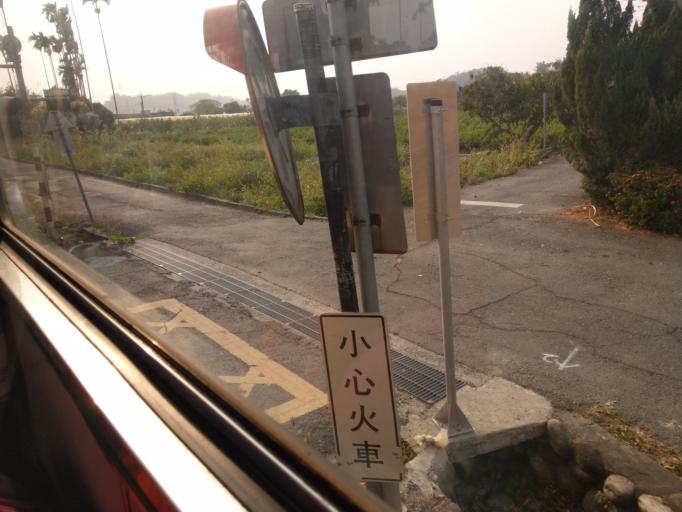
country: TW
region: Taiwan
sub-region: Chiayi
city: Jiayi Shi
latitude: 23.5098
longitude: 120.5386
